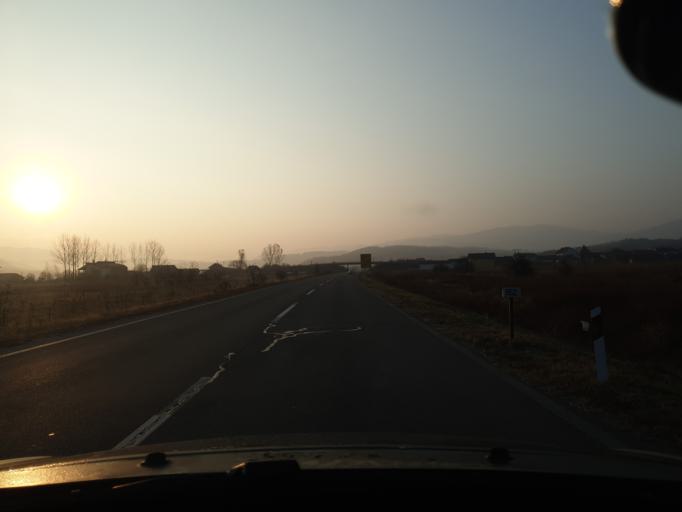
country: RS
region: Central Serbia
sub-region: Jablanicki Okrug
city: Leskovac
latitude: 42.9309
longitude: 22.0143
